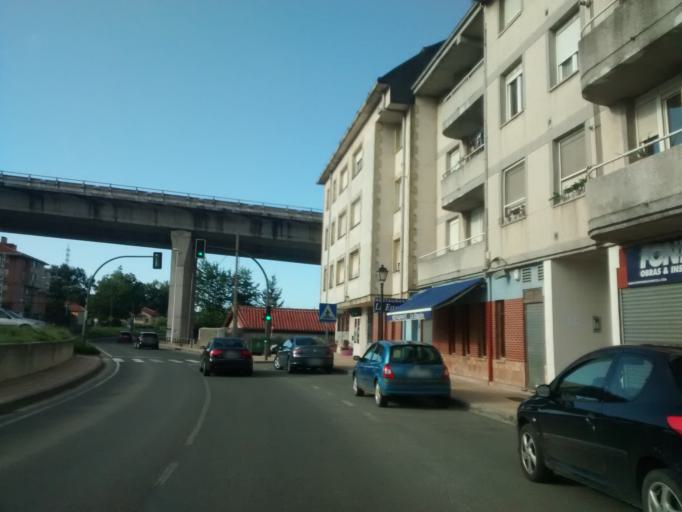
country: ES
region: Cantabria
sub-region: Provincia de Cantabria
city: Lierganes
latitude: 43.3877
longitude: -3.7309
